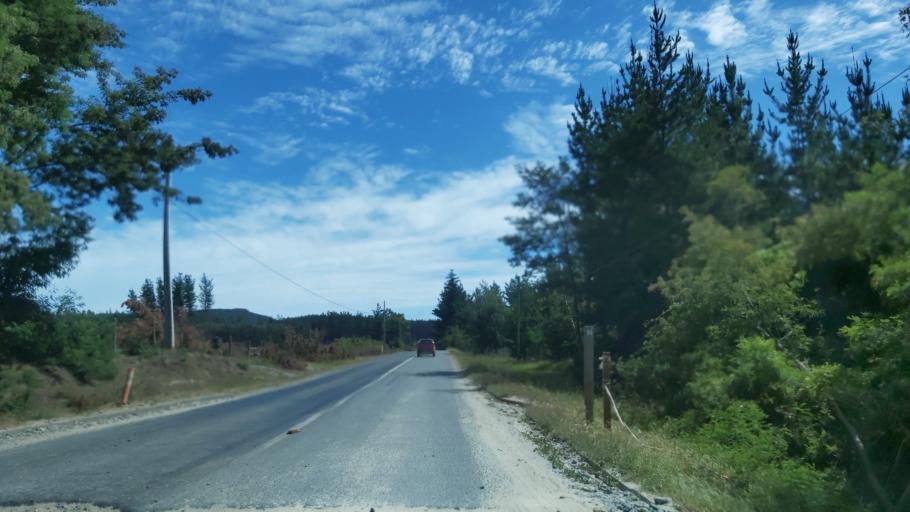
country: CL
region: Maule
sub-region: Provincia de Talca
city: Constitucion
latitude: -35.5452
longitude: -72.5618
